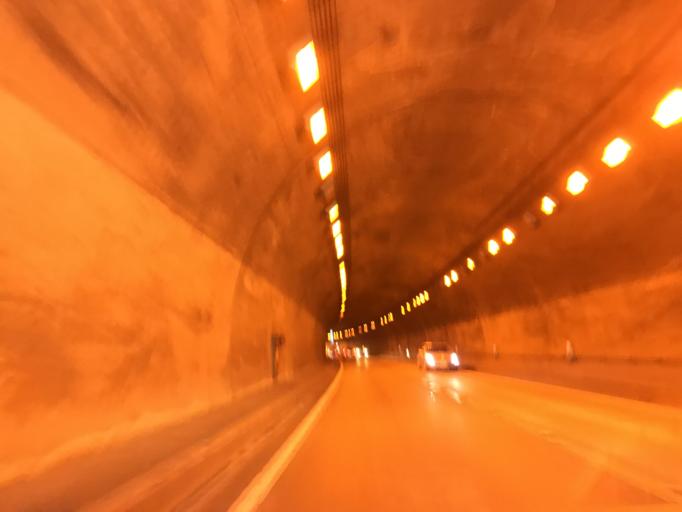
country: JP
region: Shizuoka
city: Mishima
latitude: 35.0298
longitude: 138.9234
